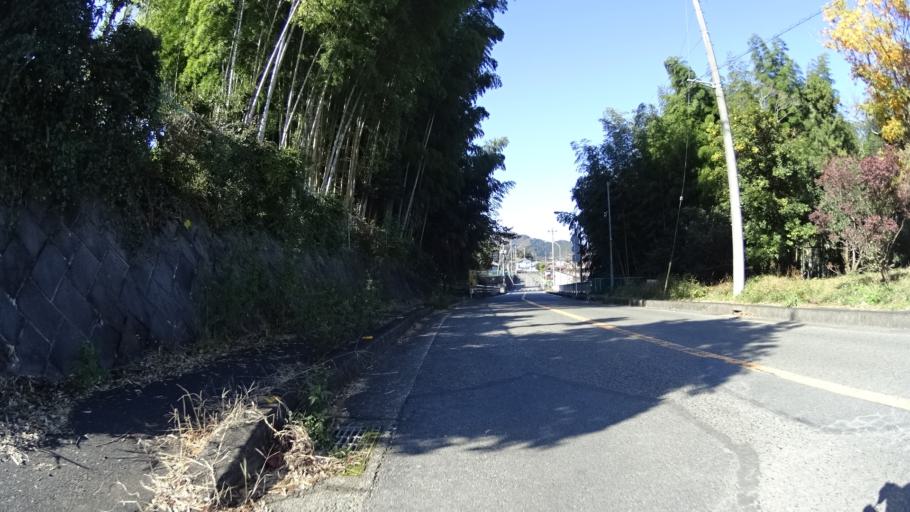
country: JP
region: Kanagawa
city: Zama
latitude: 35.5288
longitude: 139.2730
